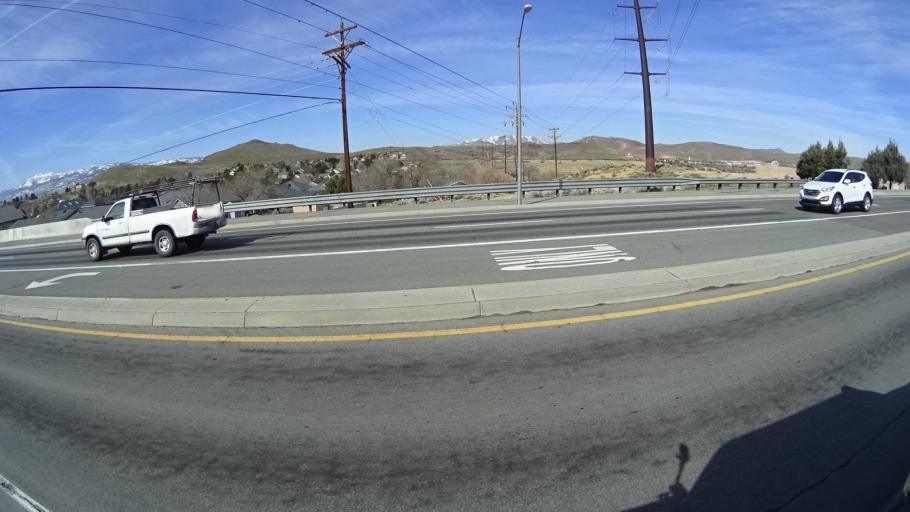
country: US
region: Nevada
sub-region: Washoe County
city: Sparks
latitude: 39.5703
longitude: -119.7237
